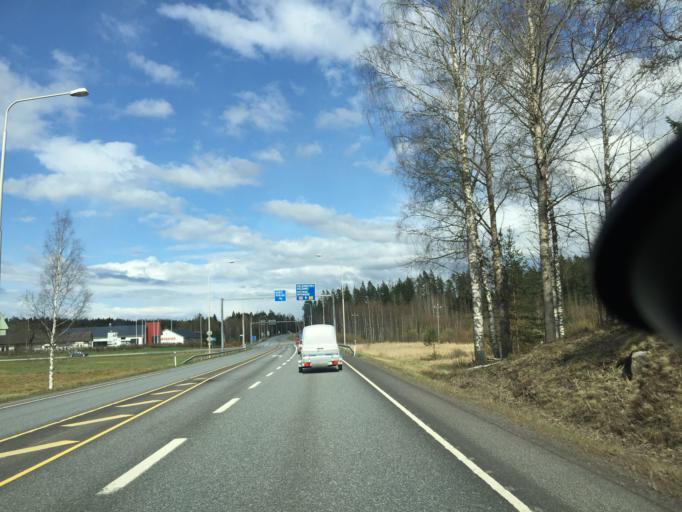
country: FI
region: Uusimaa
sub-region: Raaseporin
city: Karis
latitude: 60.0704
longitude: 23.7002
